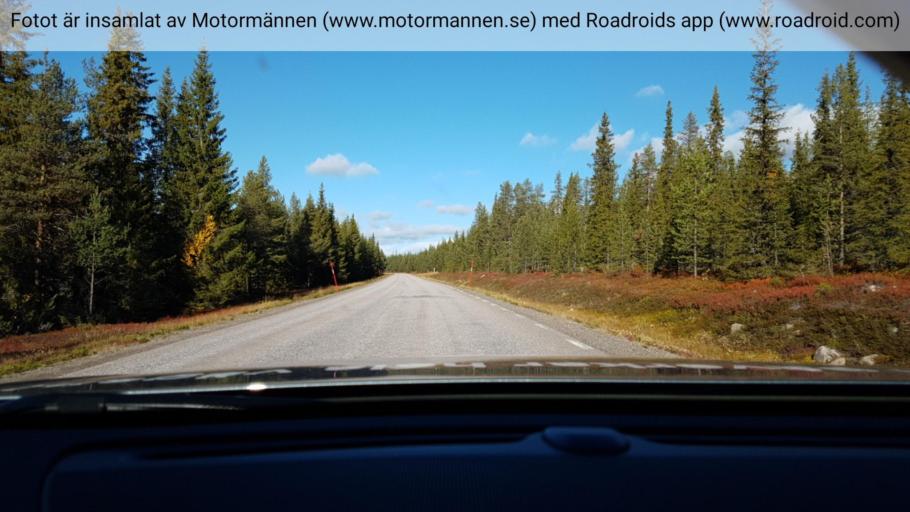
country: SE
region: Norrbotten
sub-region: Arjeplogs Kommun
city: Arjeplog
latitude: 65.8059
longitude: 18.4635
